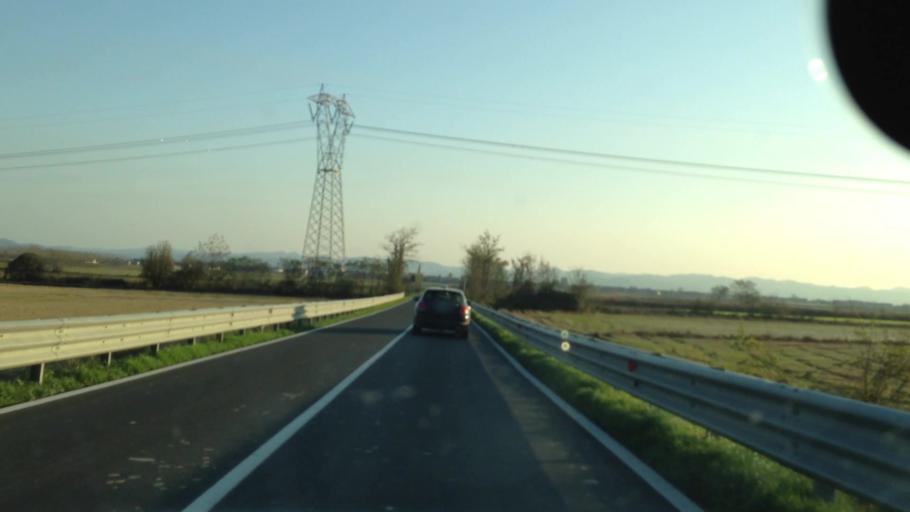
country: IT
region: Piedmont
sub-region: Provincia di Vercelli
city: Lamporo
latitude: 45.2452
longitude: 8.0905
